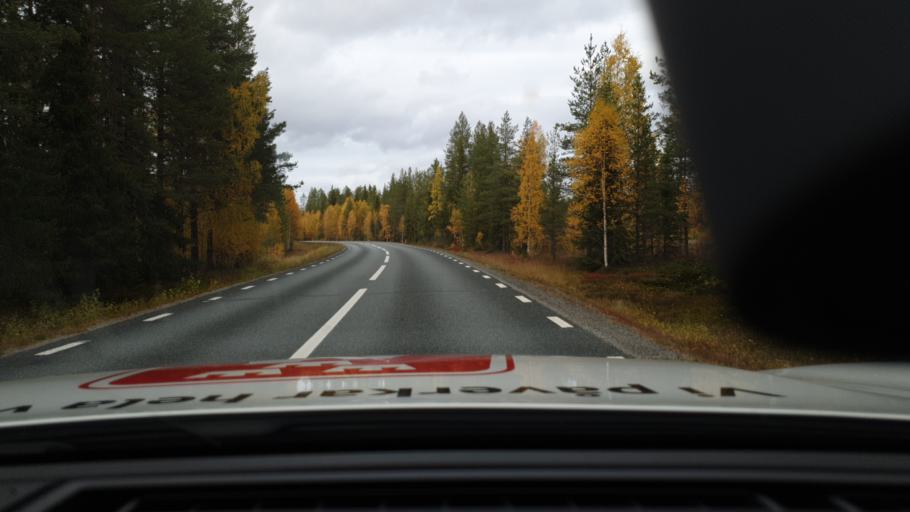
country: SE
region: Vaesterbotten
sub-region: Sorsele Kommun
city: Sorsele
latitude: 65.3824
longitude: 17.5783
